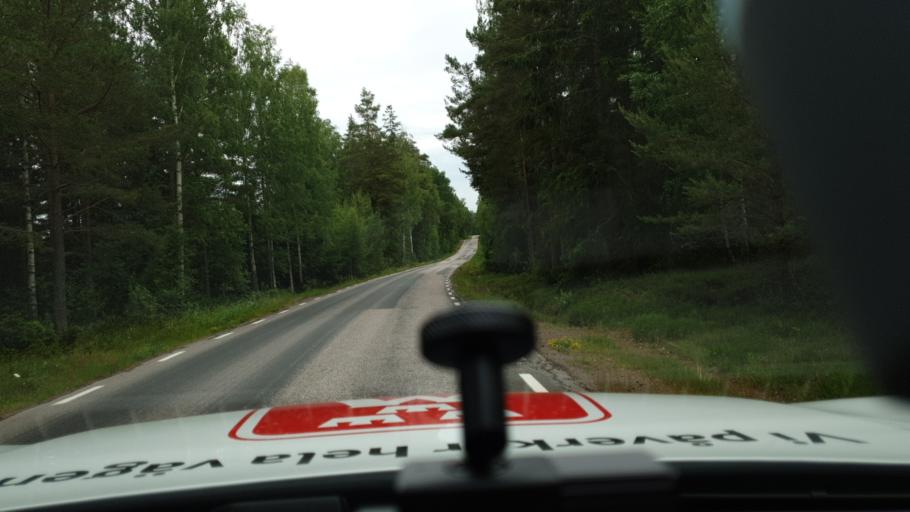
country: SE
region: Vaestra Goetaland
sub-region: Skovde Kommun
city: Stopen
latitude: 58.5644
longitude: 13.8576
